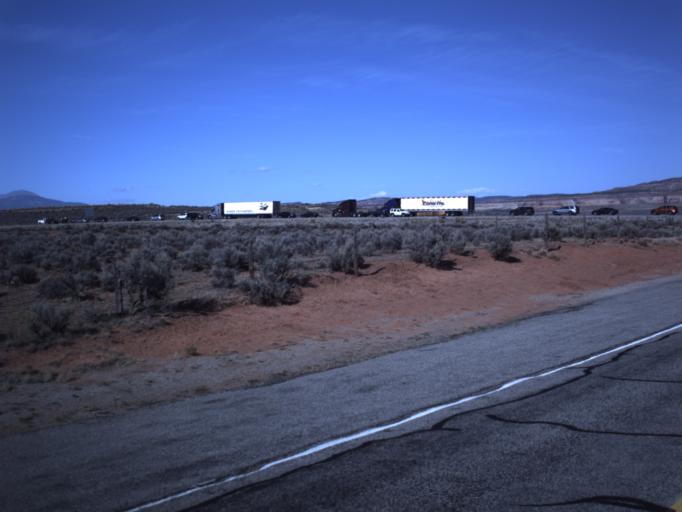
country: US
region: Utah
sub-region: San Juan County
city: Monticello
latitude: 38.0737
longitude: -109.3523
